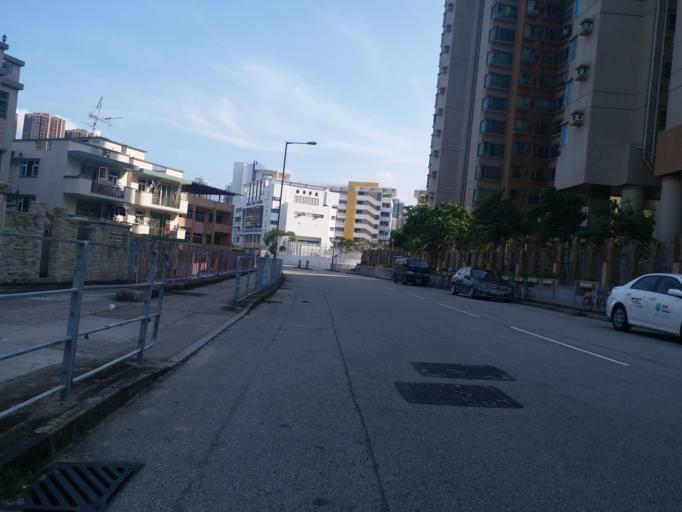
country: HK
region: Yuen Long
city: Yuen Long Kau Hui
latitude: 22.4504
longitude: 114.0335
